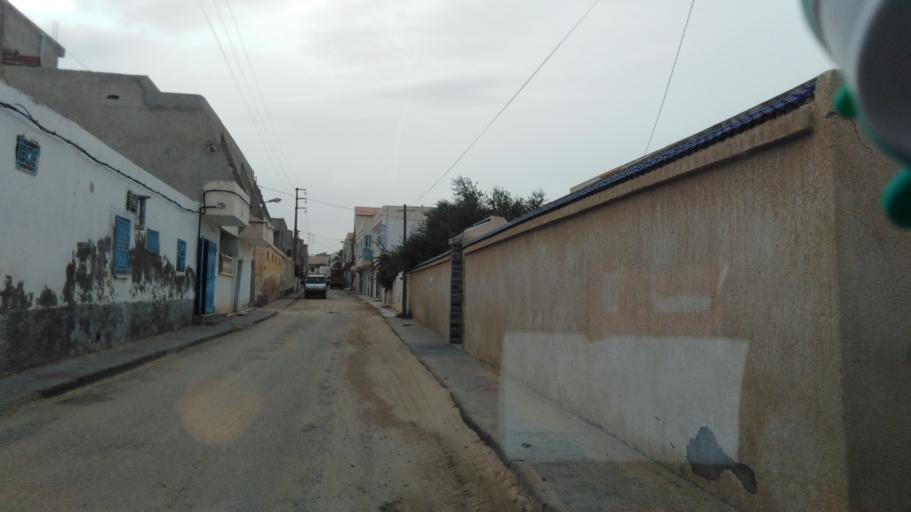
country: TN
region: Qabis
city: Gabes
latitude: 33.9576
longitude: 10.0048
